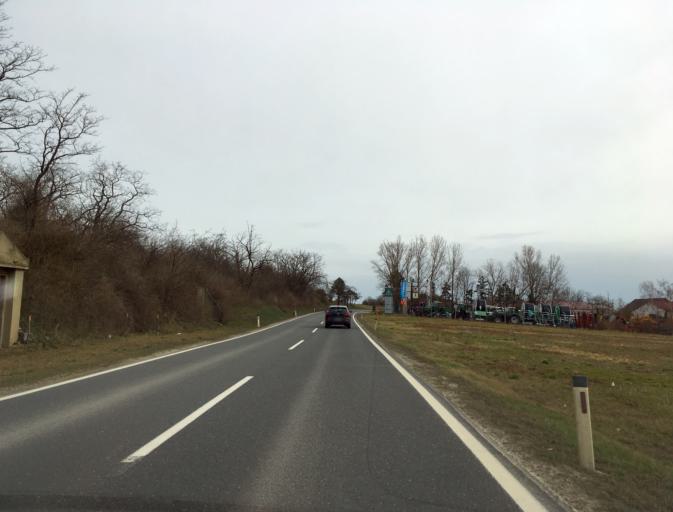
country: AT
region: Lower Austria
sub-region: Politischer Bezirk Ganserndorf
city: Parbasdorf
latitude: 48.2823
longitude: 16.5886
